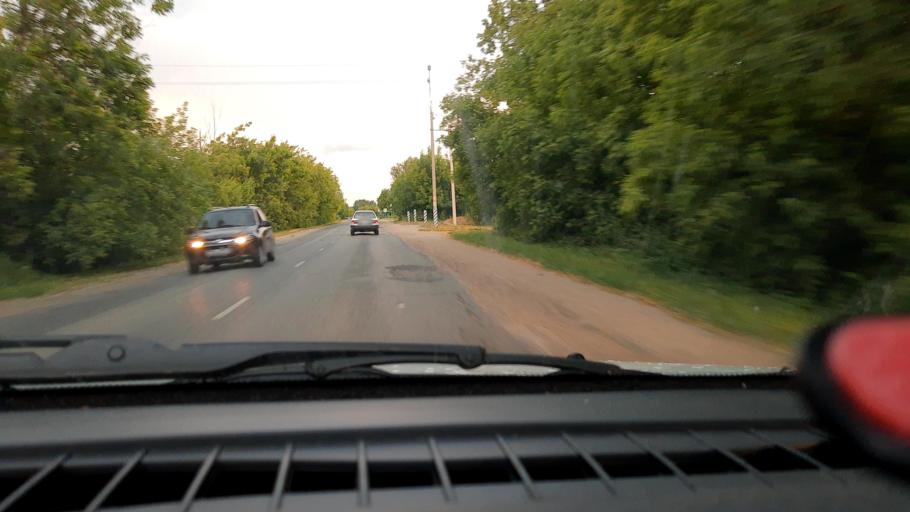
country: RU
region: Nizjnij Novgorod
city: Kstovo
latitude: 56.1332
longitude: 44.0873
